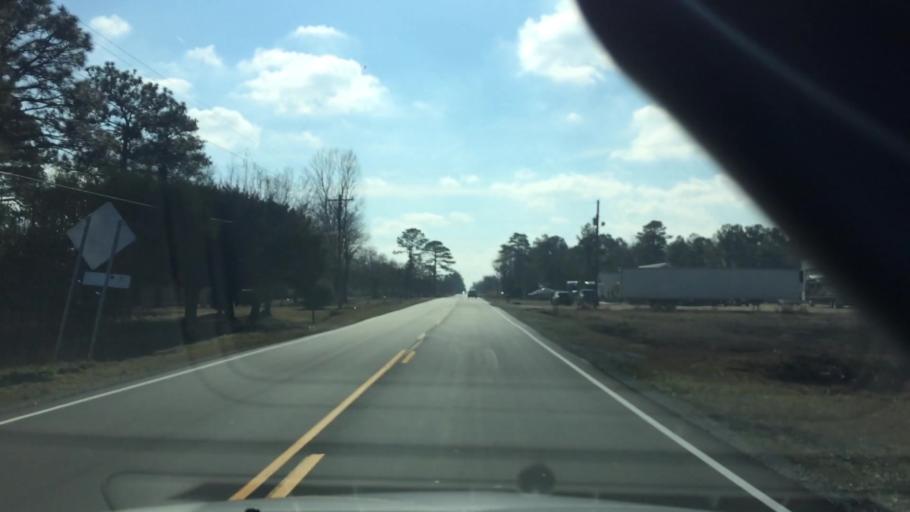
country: US
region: North Carolina
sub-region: Duplin County
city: Beulaville
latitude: 35.0006
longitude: -77.7551
